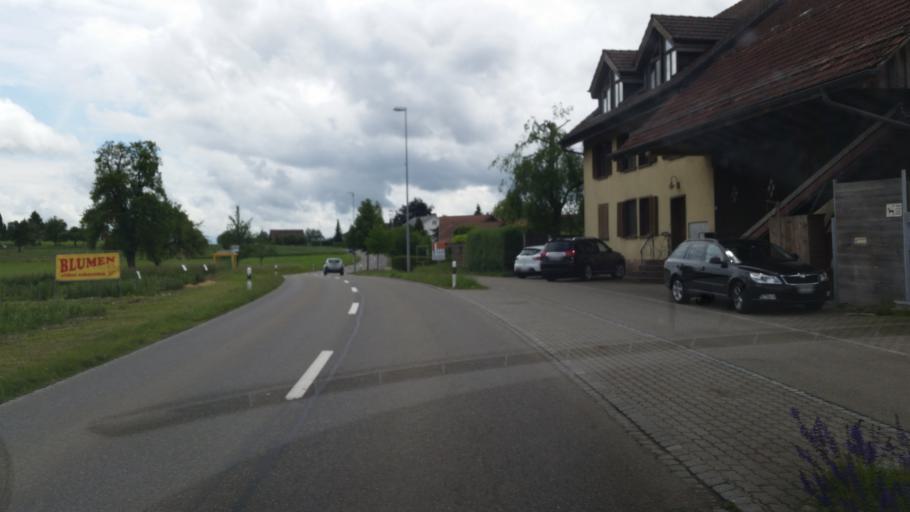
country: CH
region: Aargau
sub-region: Bezirk Bremgarten
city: Berikon
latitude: 47.3404
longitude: 8.3823
